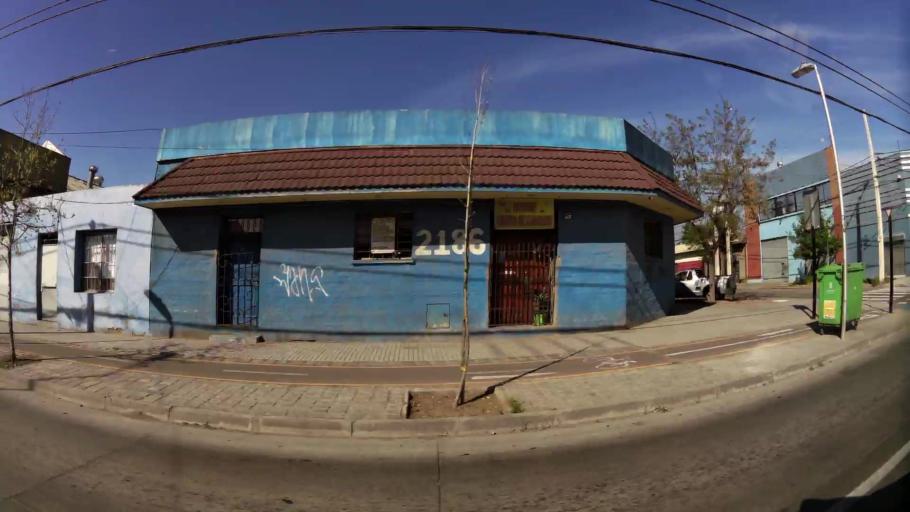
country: CL
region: Santiago Metropolitan
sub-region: Provincia de Santiago
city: Santiago
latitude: -33.4733
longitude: -70.6353
